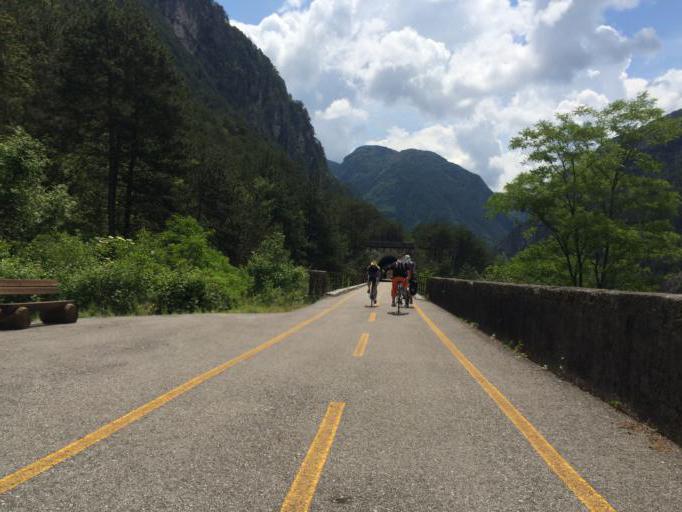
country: IT
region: Friuli Venezia Giulia
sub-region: Provincia di Udine
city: Dogna
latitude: 46.4368
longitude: 13.3126
